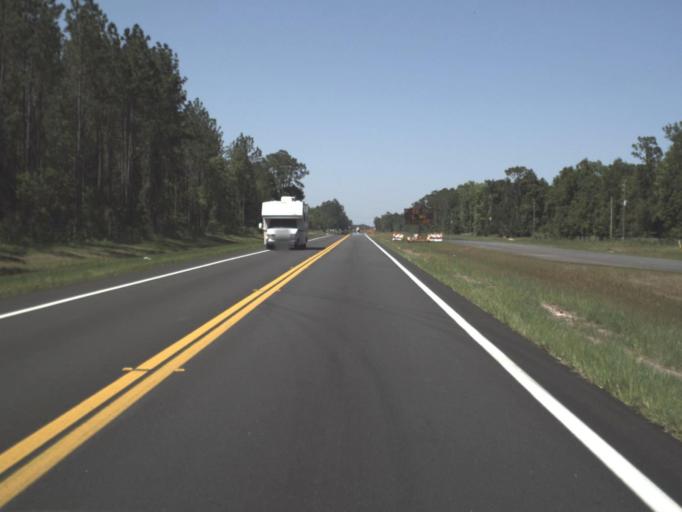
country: US
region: Florida
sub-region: Duval County
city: Baldwin
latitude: 30.3378
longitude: -81.9561
